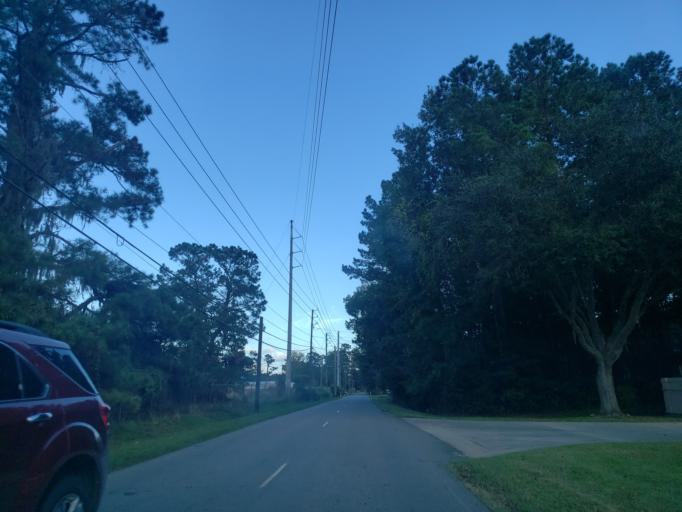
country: US
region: Georgia
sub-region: Chatham County
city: Georgetown
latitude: 31.9906
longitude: -81.2308
